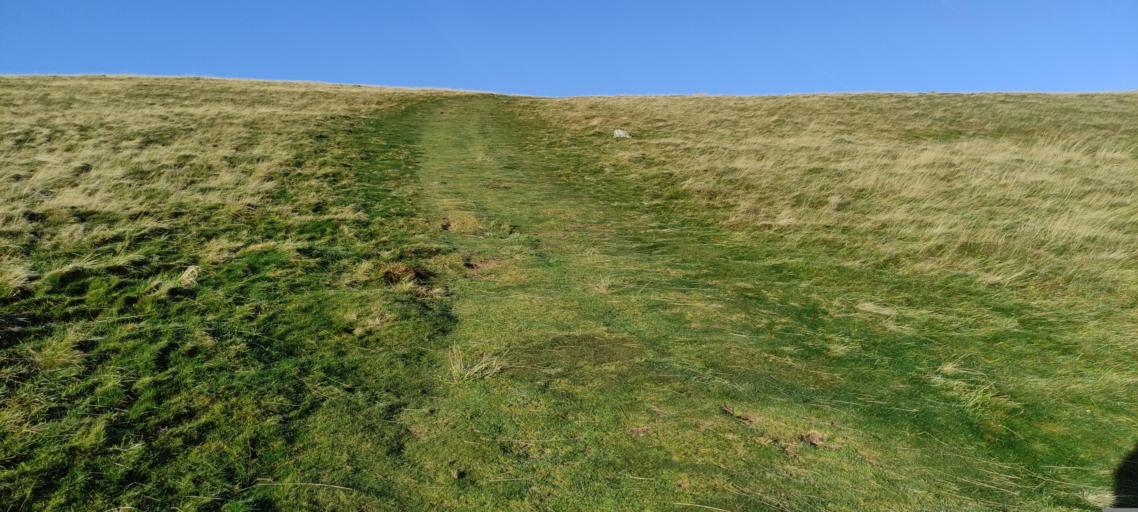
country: GB
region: England
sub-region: Cumbria
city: Wigton
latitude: 54.7069
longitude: -3.1947
